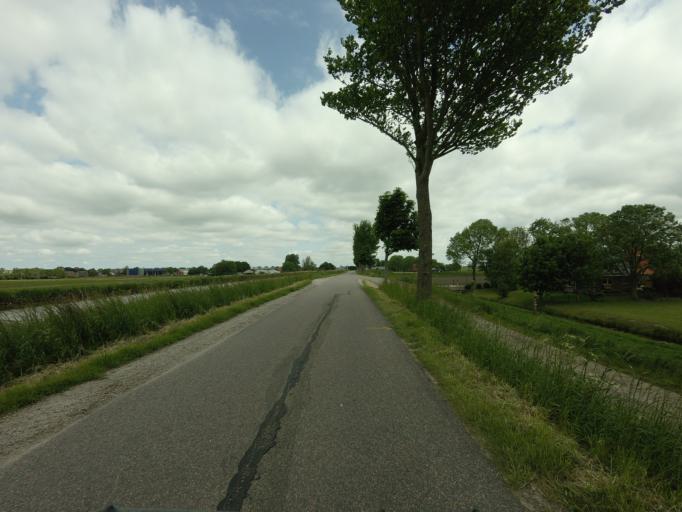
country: NL
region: North Holland
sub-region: Gemeente Beemster
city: Halfweg
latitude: 52.5442
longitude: 4.8430
